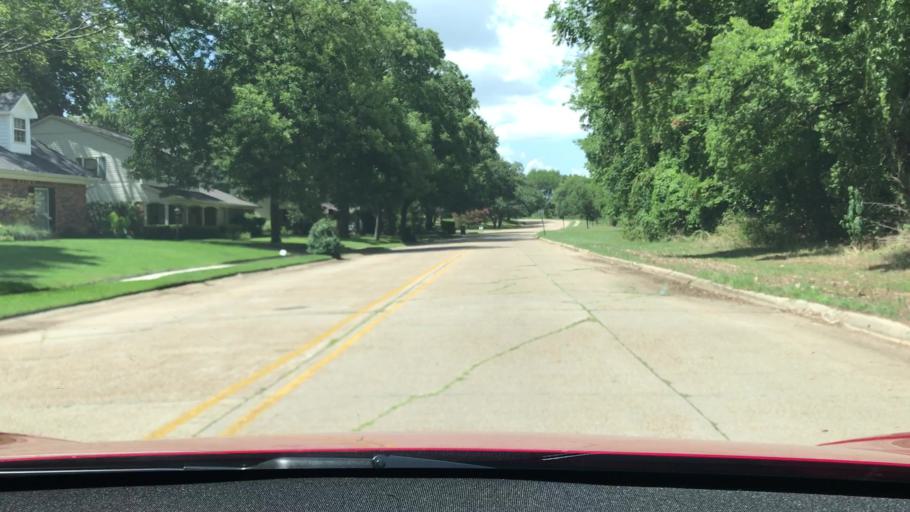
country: US
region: Louisiana
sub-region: Bossier Parish
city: Bossier City
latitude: 32.4309
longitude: -93.7282
